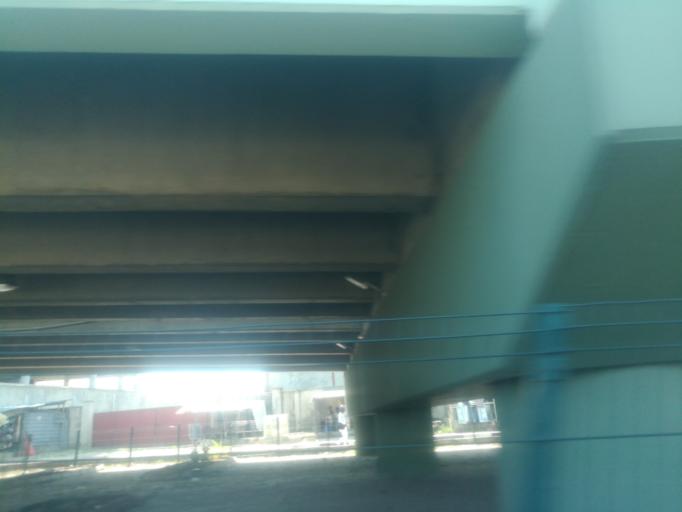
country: NG
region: Ogun
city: Abeokuta
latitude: 7.1377
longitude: 3.3326
